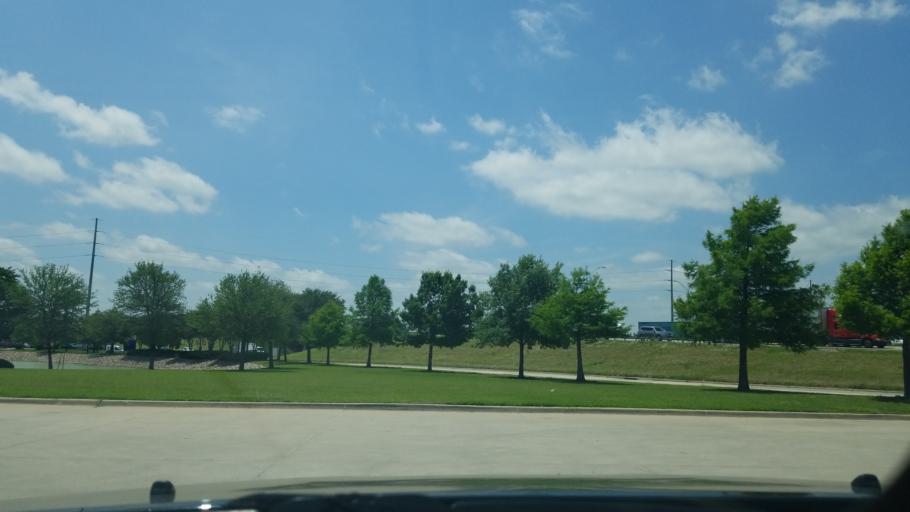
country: US
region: Texas
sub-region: Denton County
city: Denton
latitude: 33.2172
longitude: -97.1687
